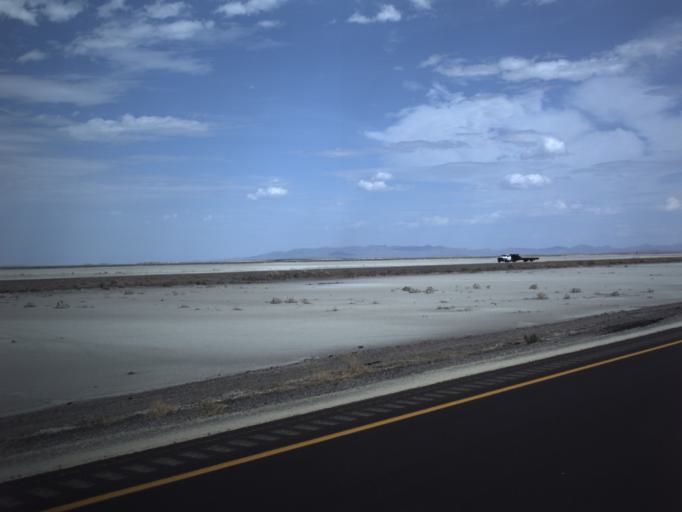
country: US
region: Utah
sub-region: Tooele County
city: Wendover
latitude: 40.7304
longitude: -113.4778
